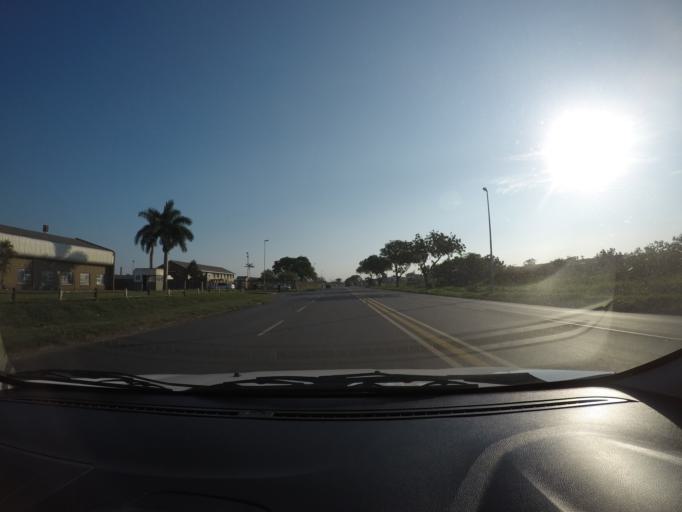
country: ZA
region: KwaZulu-Natal
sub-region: uThungulu District Municipality
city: Richards Bay
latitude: -28.7581
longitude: 32.0246
